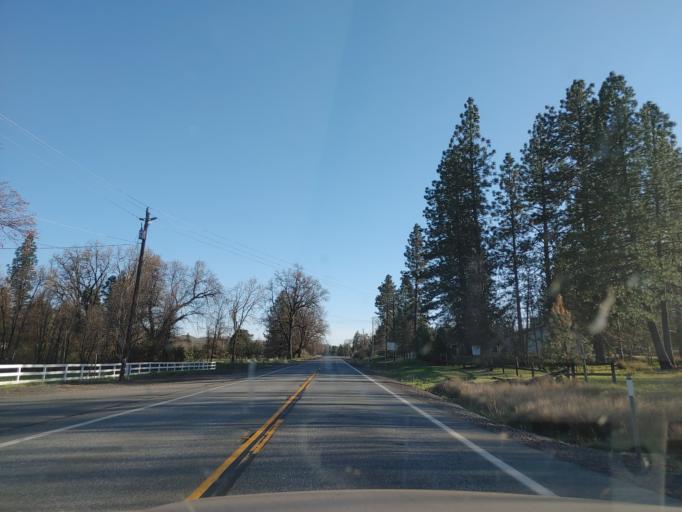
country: US
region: California
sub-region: Shasta County
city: Burney
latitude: 40.8113
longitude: -121.9393
